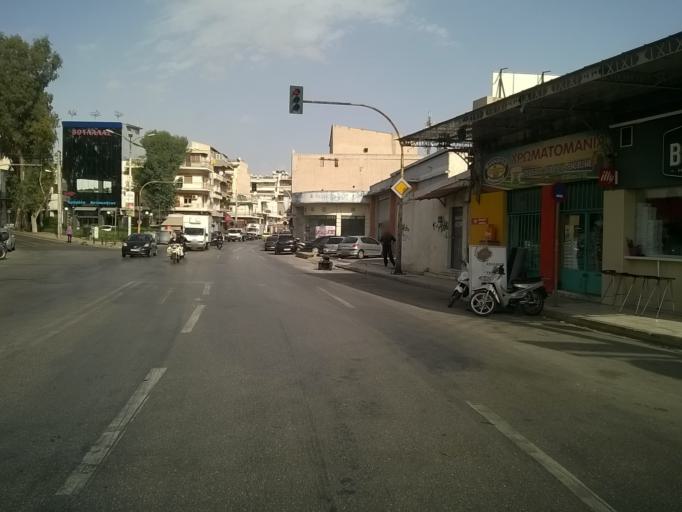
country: GR
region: Attica
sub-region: Nomos Piraios
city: Nikaia
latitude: 37.9556
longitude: 23.6497
